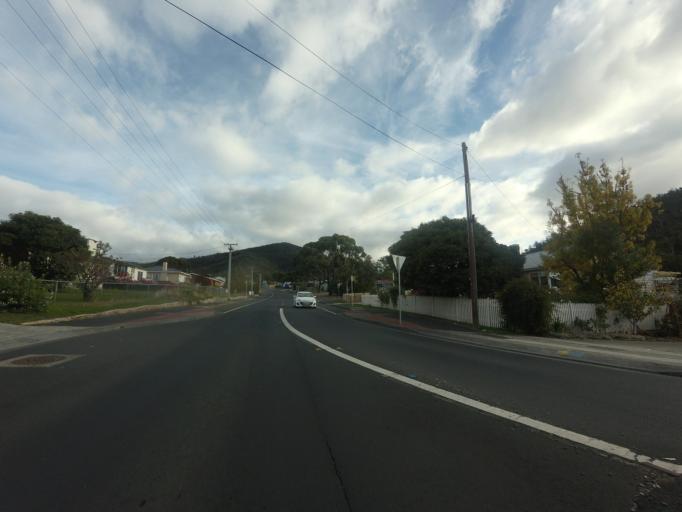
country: AU
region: Tasmania
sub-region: Glenorchy
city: Berriedale
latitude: -42.8100
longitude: 147.2431
